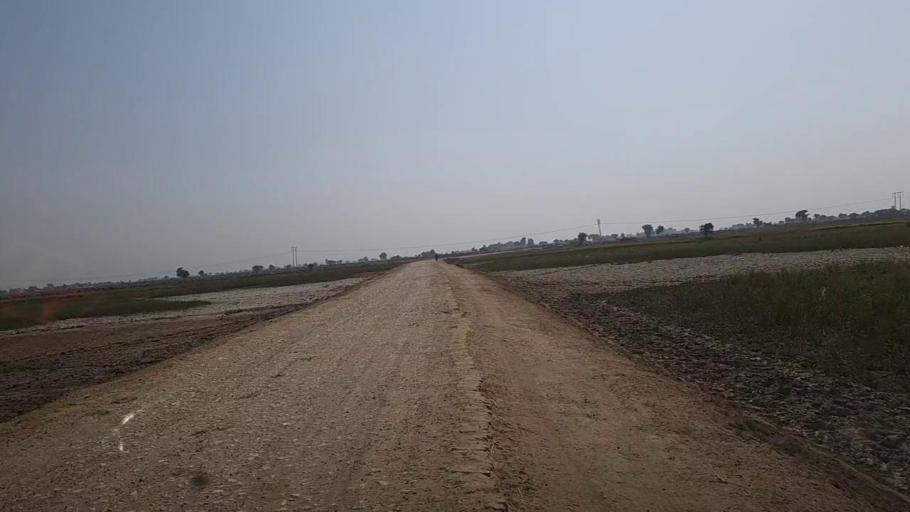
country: PK
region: Sindh
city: Kandhkot
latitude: 28.3919
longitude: 69.2933
